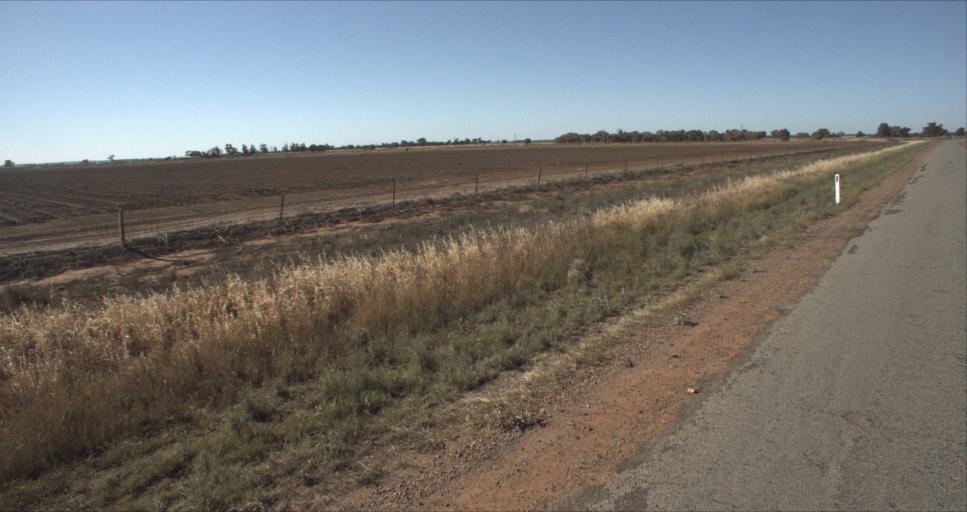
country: AU
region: New South Wales
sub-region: Leeton
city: Leeton
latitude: -34.5641
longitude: 146.3121
